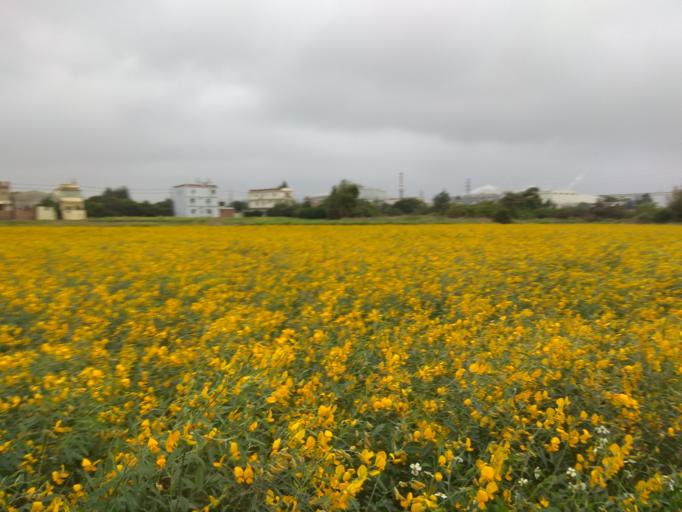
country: TW
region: Taiwan
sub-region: Hsinchu
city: Zhubei
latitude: 24.9854
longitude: 121.0393
